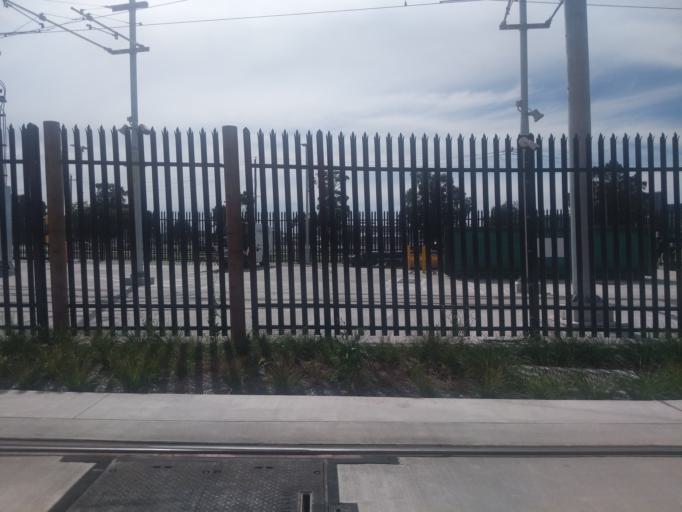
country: AU
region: New South Wales
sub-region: Newcastle
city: Carrington
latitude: -32.9252
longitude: 151.7617
